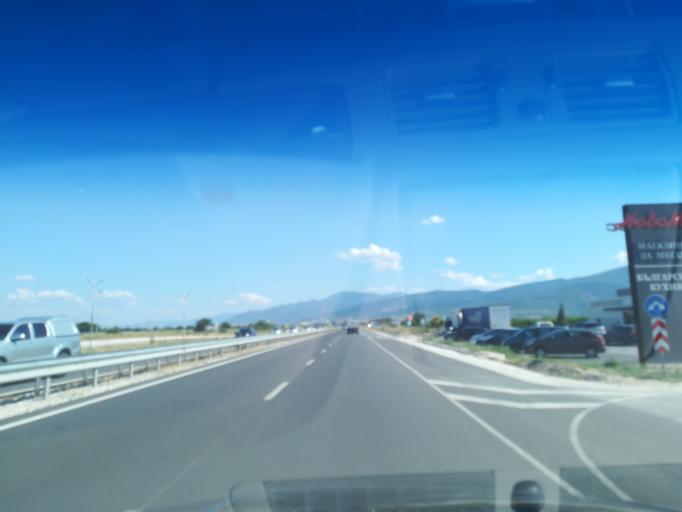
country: BG
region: Plovdiv
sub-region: Obshtina Plovdiv
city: Plovdiv
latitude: 42.0895
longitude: 24.7945
